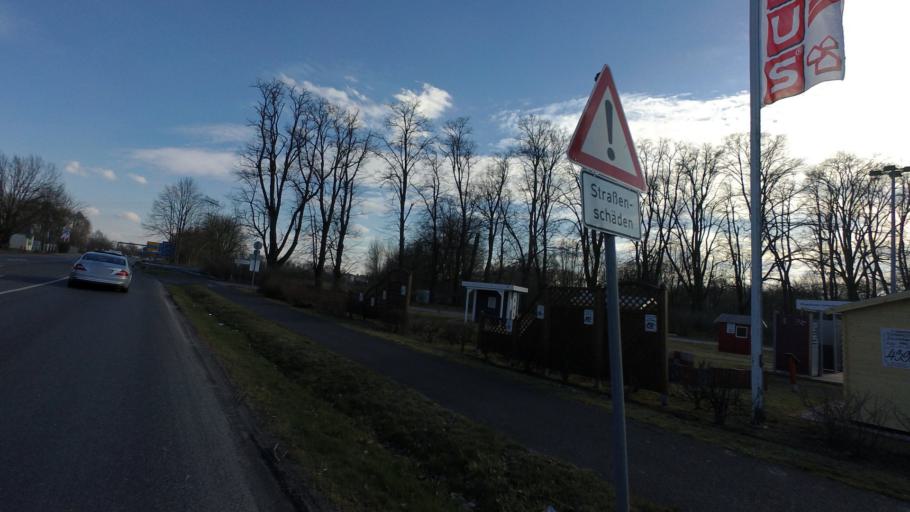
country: DE
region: Brandenburg
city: Birkenwerder
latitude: 52.7036
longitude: 13.2713
